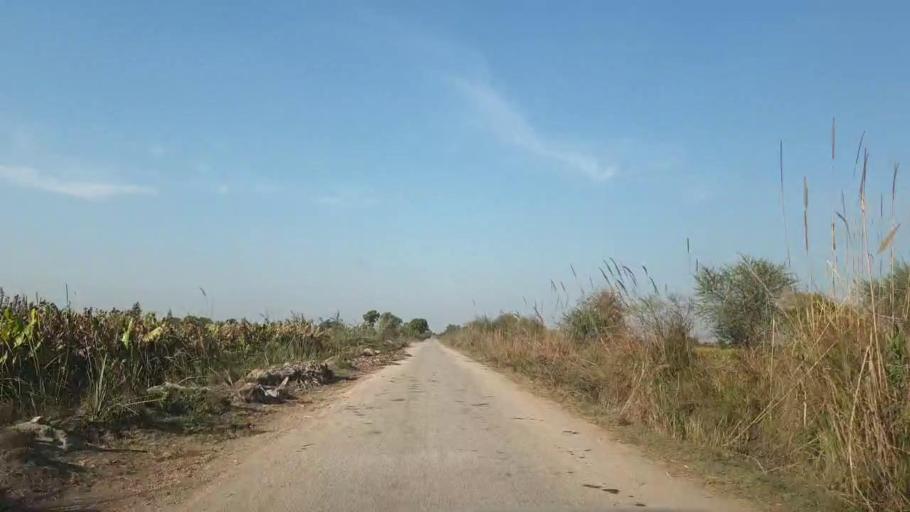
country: PK
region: Sindh
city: Tando Adam
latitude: 25.7211
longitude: 68.7031
